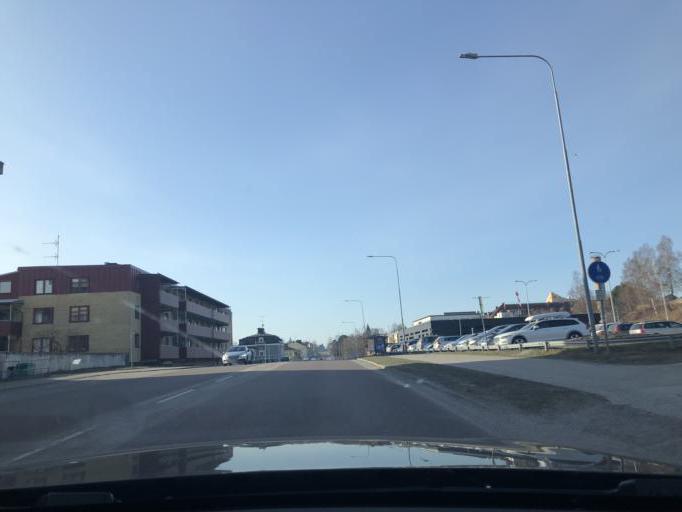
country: SE
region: Gaevleborg
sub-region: Hudiksvalls Kommun
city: Hudiksvall
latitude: 61.7322
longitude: 17.1000
